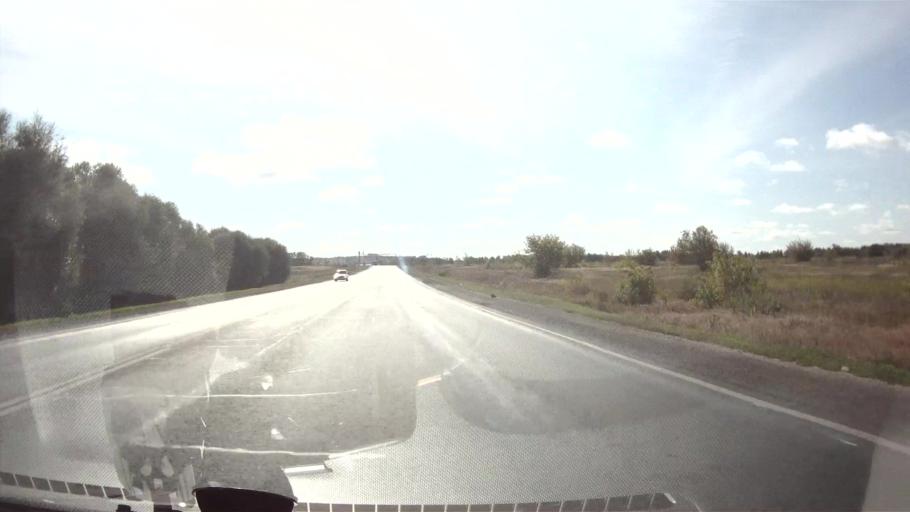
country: RU
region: Ulyanovsk
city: Isheyevka
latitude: 54.3016
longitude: 48.2436
